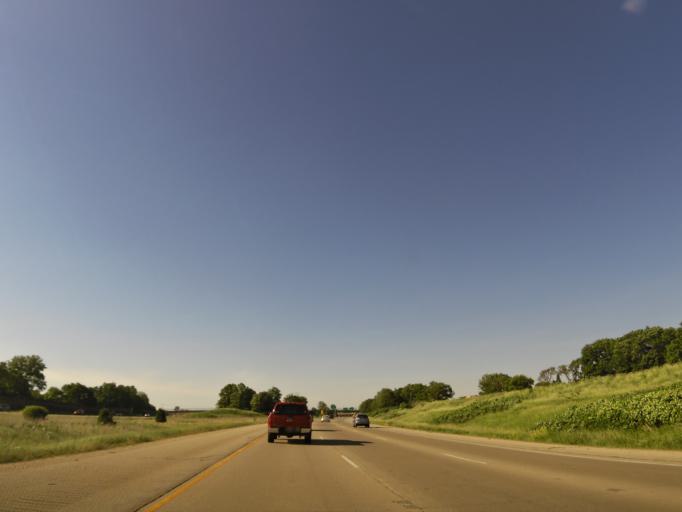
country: US
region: Wisconsin
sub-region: Dane County
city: Monona
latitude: 43.0940
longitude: -89.2855
